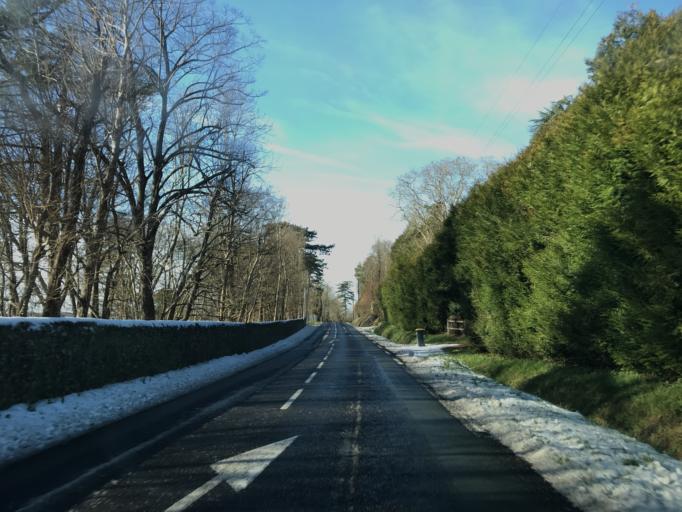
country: FR
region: Haute-Normandie
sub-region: Departement de l'Eure
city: Houlbec-Cocherel
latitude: 49.0620
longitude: 1.3285
